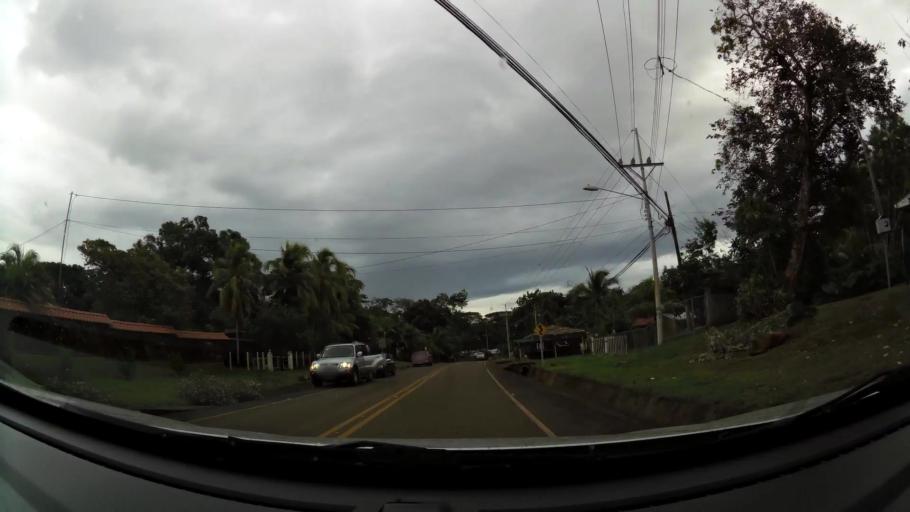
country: CR
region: Alajuela
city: Orotina
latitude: 9.9578
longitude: -84.5882
